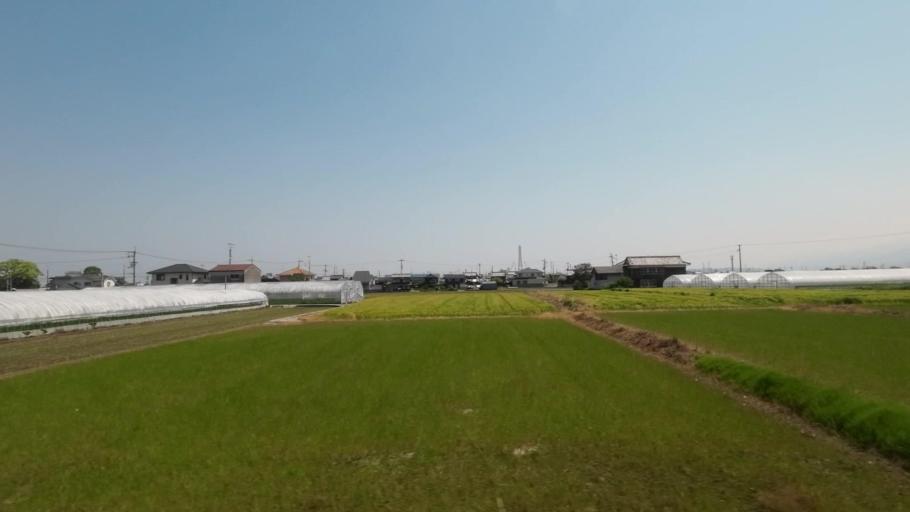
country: JP
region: Ehime
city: Saijo
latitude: 33.9234
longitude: 133.0911
